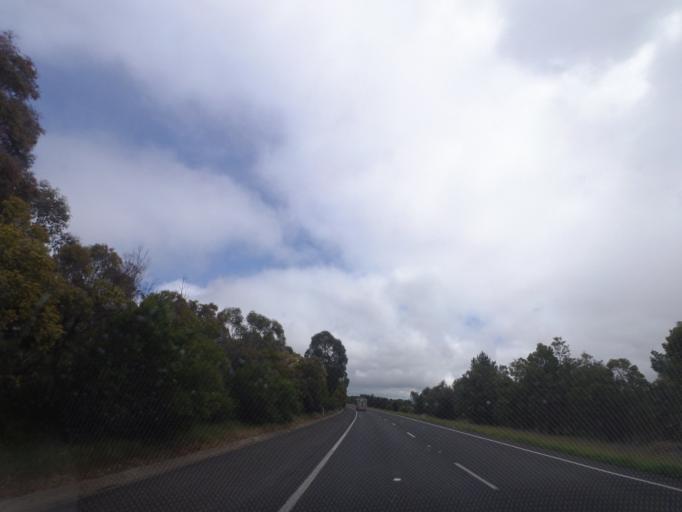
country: AU
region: Victoria
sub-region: Ballarat North
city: Soldiers Hill
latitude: -37.5236
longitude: 143.8639
